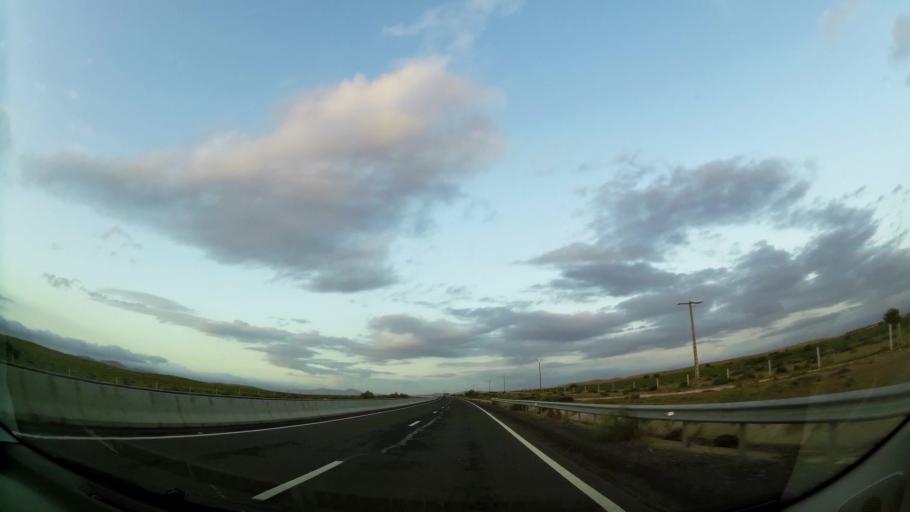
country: MA
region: Oriental
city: Taourirt
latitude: 34.5507
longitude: -2.8601
